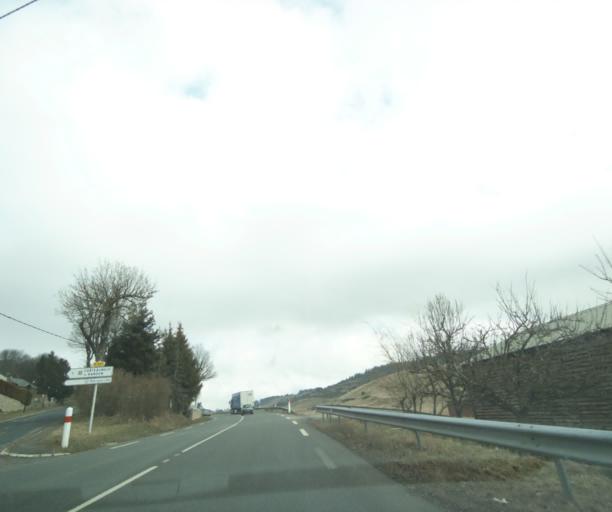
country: FR
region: Languedoc-Roussillon
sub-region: Departement de la Lozere
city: Langogne
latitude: 44.6343
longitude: 3.6767
